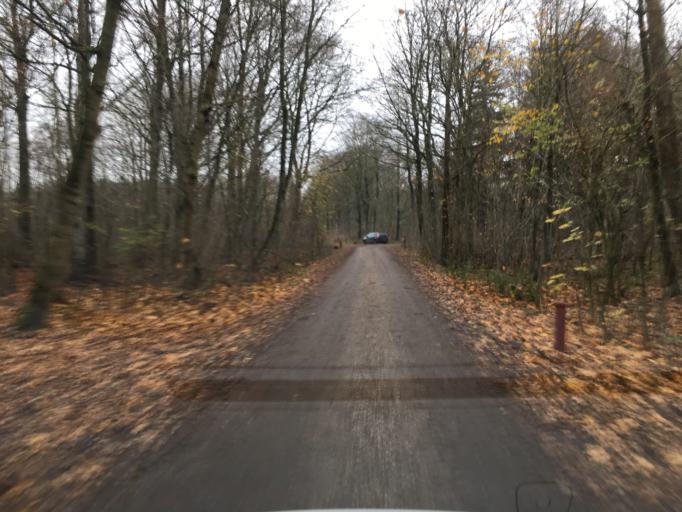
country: DK
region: South Denmark
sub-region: Tonder Kommune
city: Tonder
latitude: 54.9630
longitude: 8.8563
